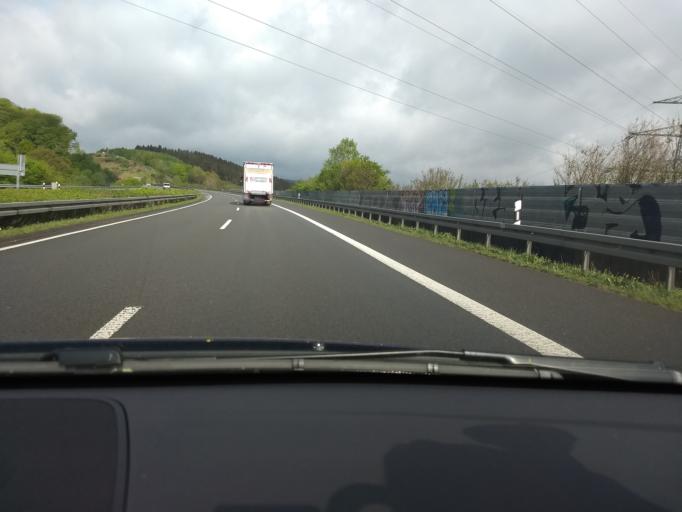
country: DE
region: North Rhine-Westphalia
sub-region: Regierungsbezirk Arnsberg
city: Arnsberg
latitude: 51.3808
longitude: 8.1515
